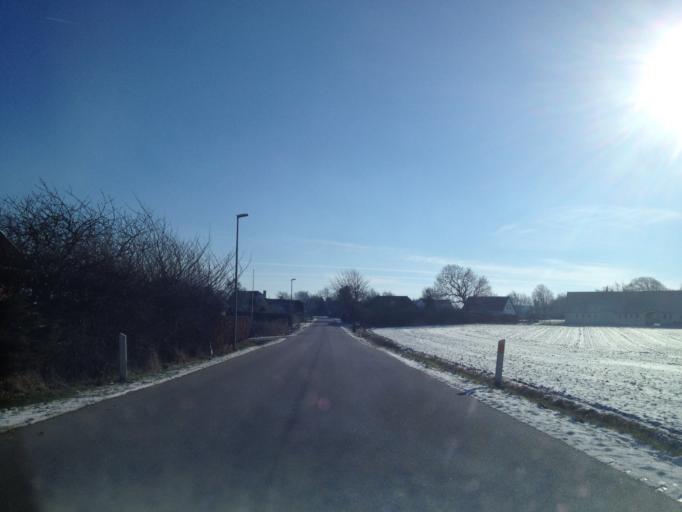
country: DK
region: South Denmark
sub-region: Haderslev Kommune
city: Haderslev
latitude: 55.2913
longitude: 9.4396
